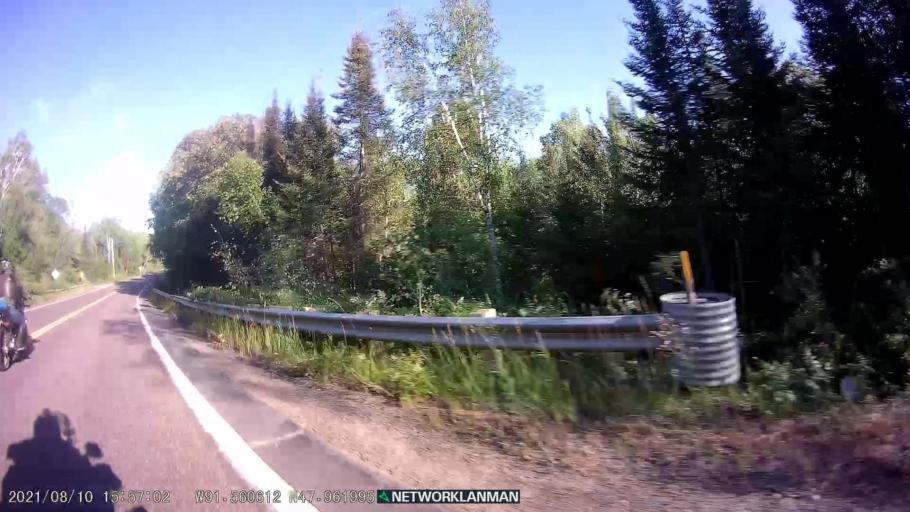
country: US
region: Minnesota
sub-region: Saint Louis County
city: Ely
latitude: 47.9619
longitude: -91.5600
